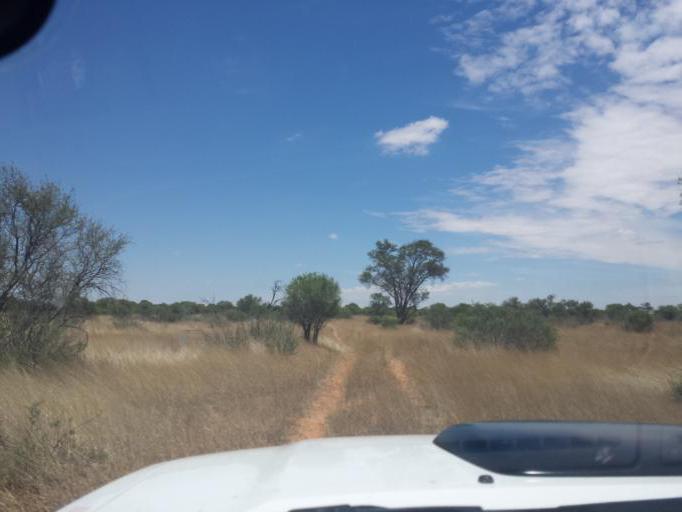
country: BW
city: Lokwabe
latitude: -24.9139
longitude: 21.6073
